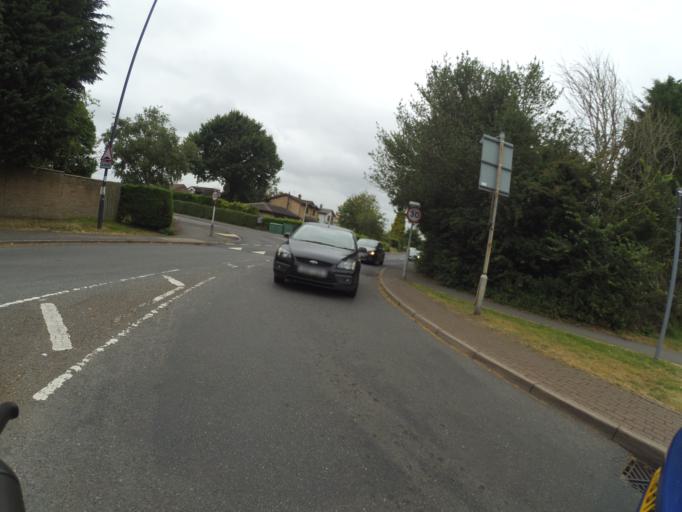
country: GB
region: England
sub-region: Warwickshire
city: Dunchurch
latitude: 52.3499
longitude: -1.2770
